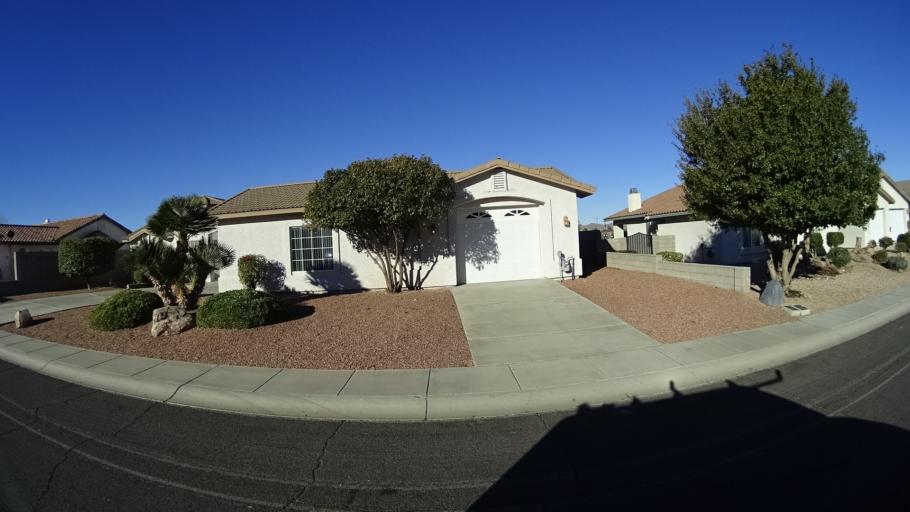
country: US
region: Arizona
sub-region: Mohave County
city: Kingman
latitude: 35.1936
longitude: -114.0066
